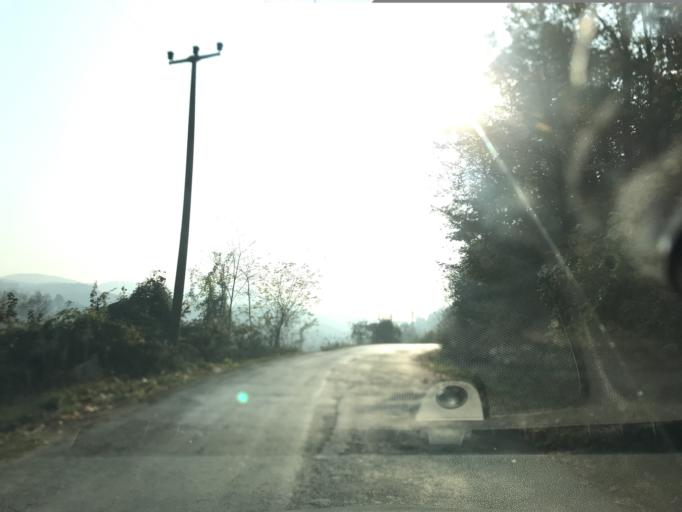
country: TR
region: Duzce
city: Cumayeri
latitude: 40.9122
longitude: 30.9439
